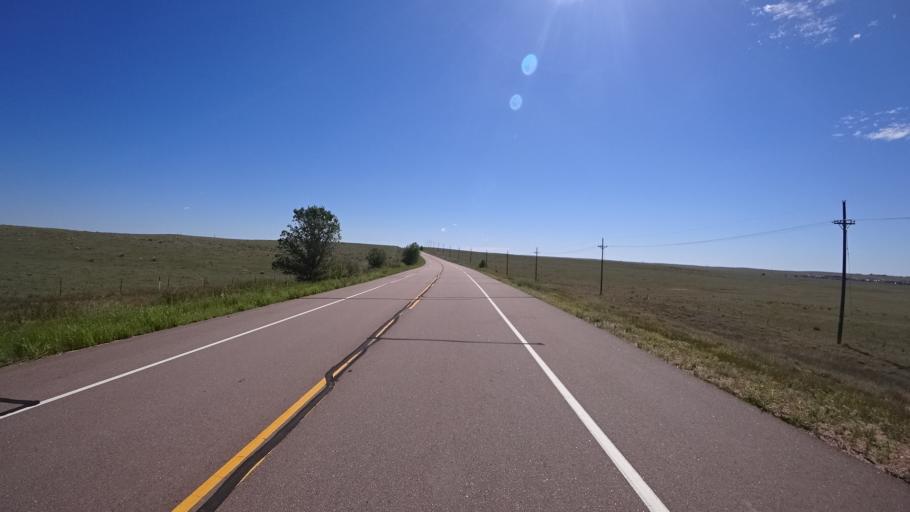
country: US
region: Colorado
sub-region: El Paso County
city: Security-Widefield
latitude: 38.7614
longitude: -104.6437
